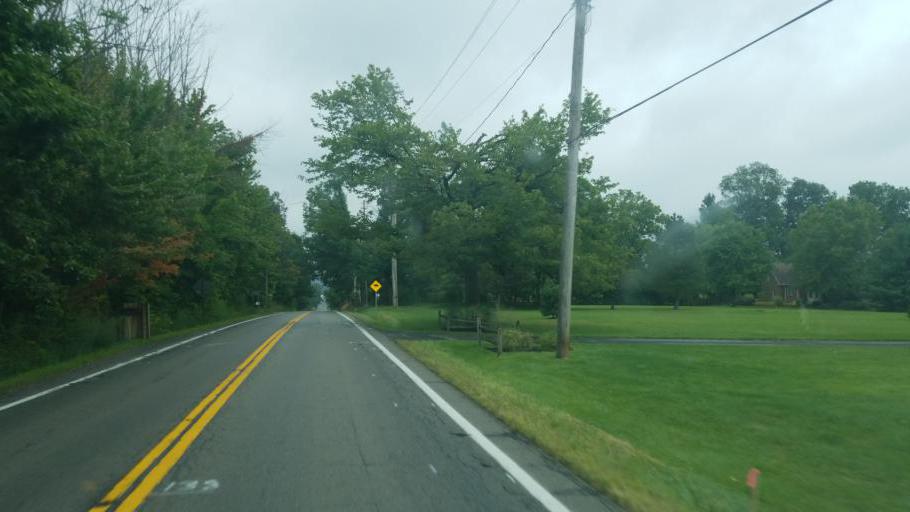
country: US
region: Ohio
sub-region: Geauga County
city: Burton
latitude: 41.4242
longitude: -81.2102
